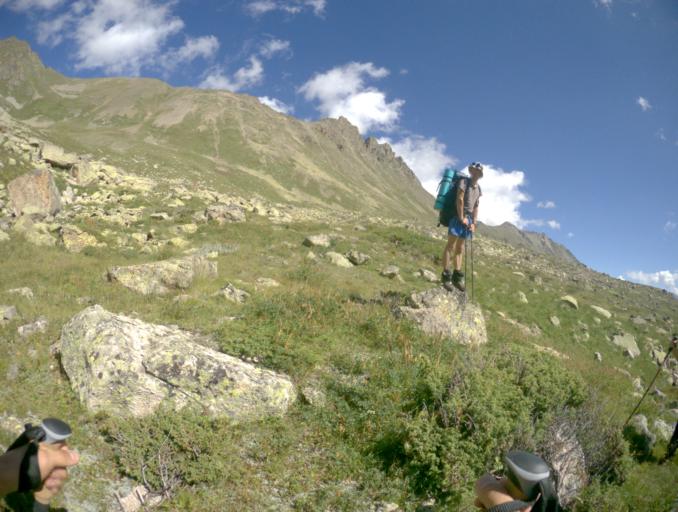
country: RU
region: Karachayevo-Cherkesiya
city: Uchkulan
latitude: 43.3251
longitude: 42.1000
